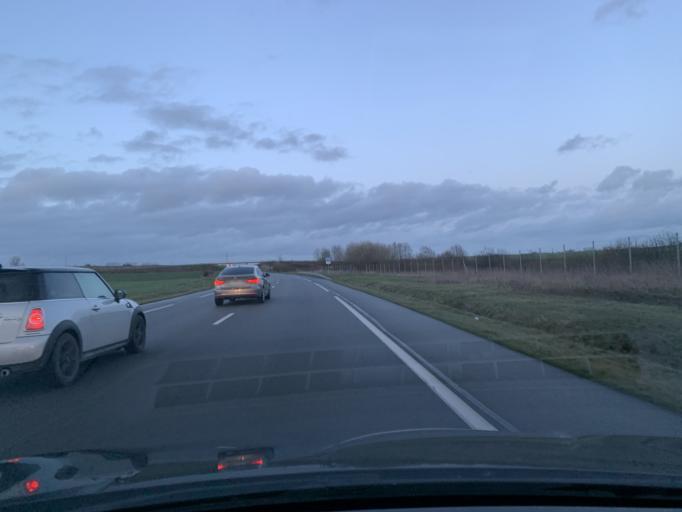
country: FR
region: Nord-Pas-de-Calais
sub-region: Departement du Nord
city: Escaudoeuvres
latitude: 50.1525
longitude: 3.2913
